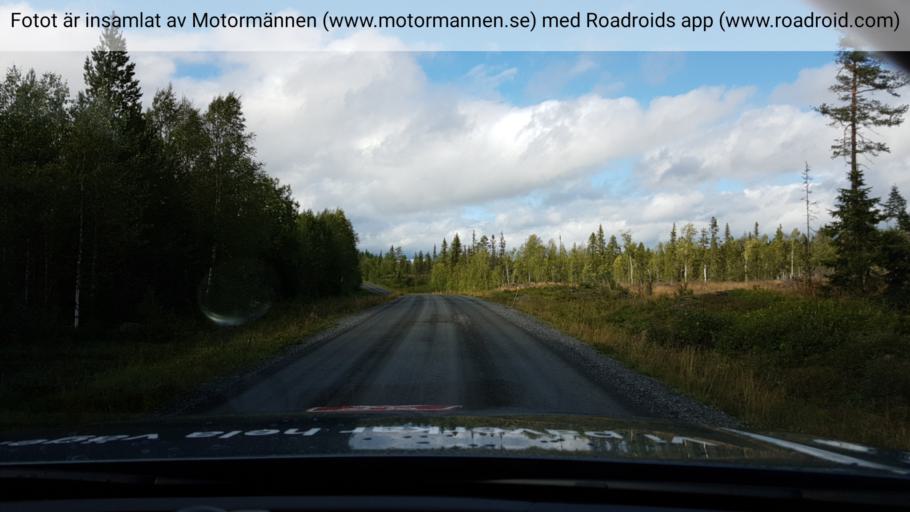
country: SE
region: Jaemtland
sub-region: Krokoms Kommun
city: Krokom
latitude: 63.7227
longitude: 14.5150
